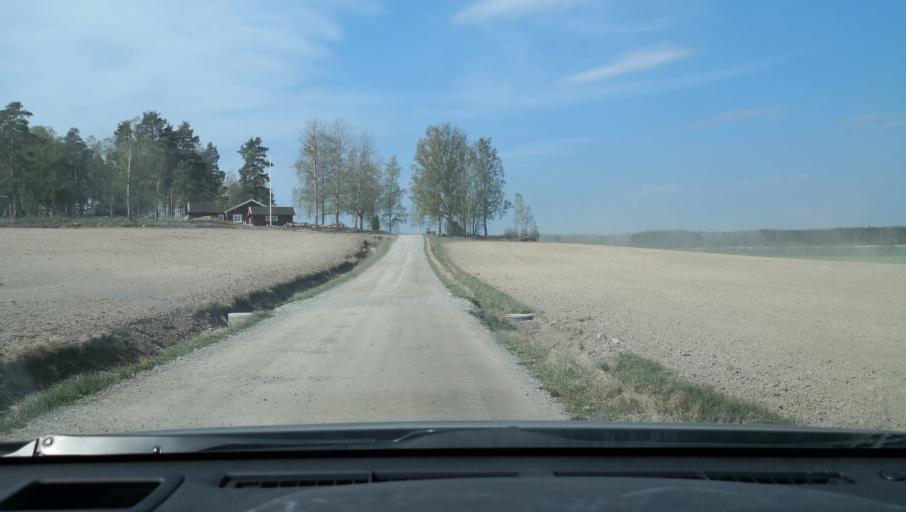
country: SE
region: Vaestmanland
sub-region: Vasteras
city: Skultuna
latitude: 59.7749
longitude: 16.4349
